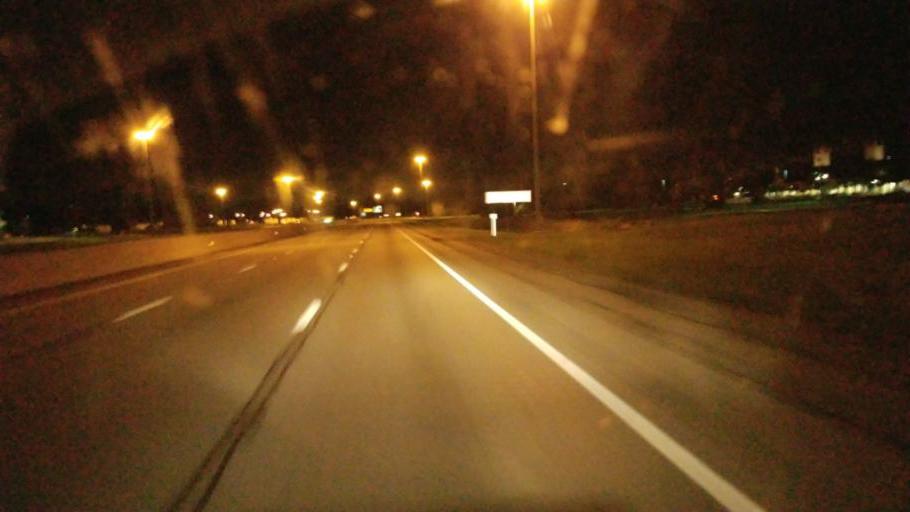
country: US
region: Ohio
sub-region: Licking County
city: Harbor Hills
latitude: 39.9467
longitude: -82.4509
